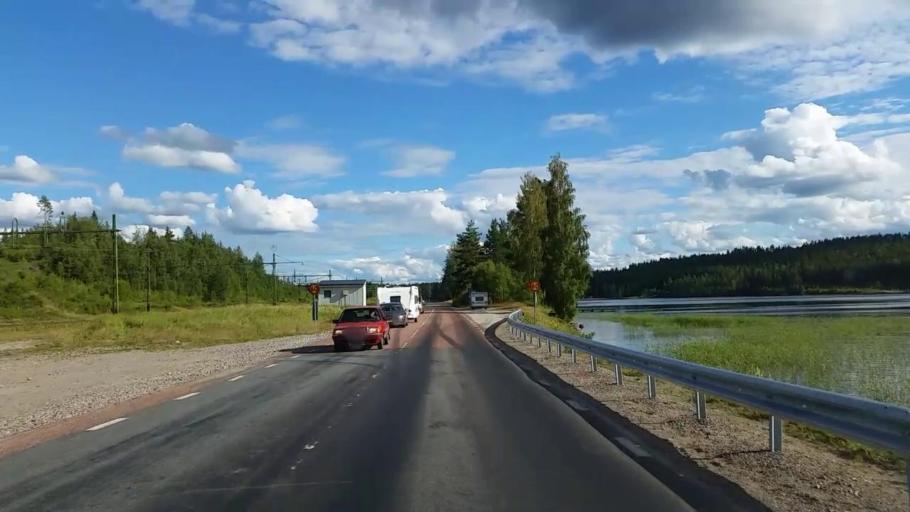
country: SE
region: Gaevleborg
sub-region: Ljusdals Kommun
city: Farila
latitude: 62.0235
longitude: 15.9005
